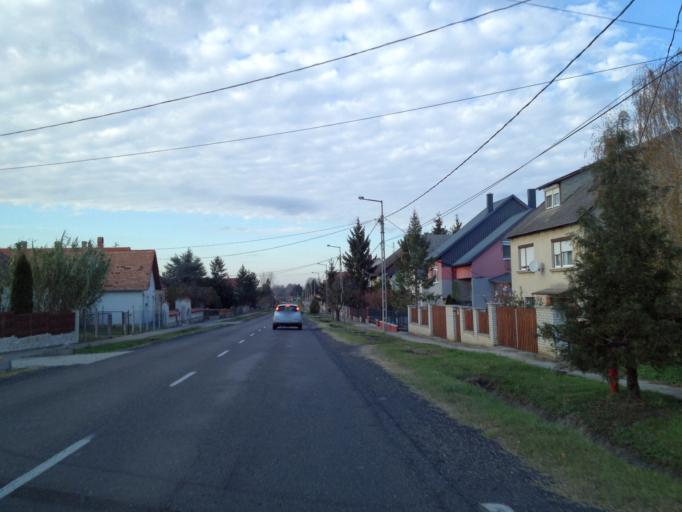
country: HU
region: Gyor-Moson-Sopron
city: Bakonyszentlaszlo
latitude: 47.4363
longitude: 17.8237
